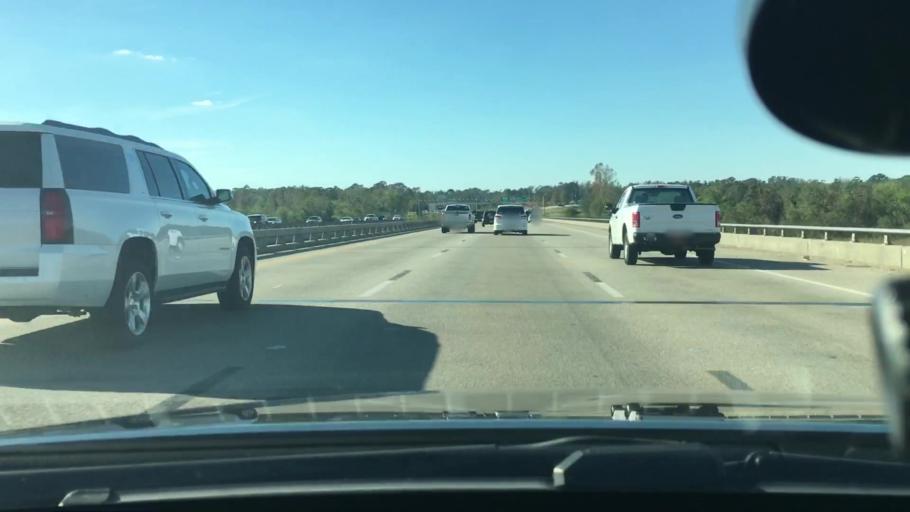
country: US
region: North Carolina
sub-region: Craven County
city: New Bern
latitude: 35.0981
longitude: -77.0500
